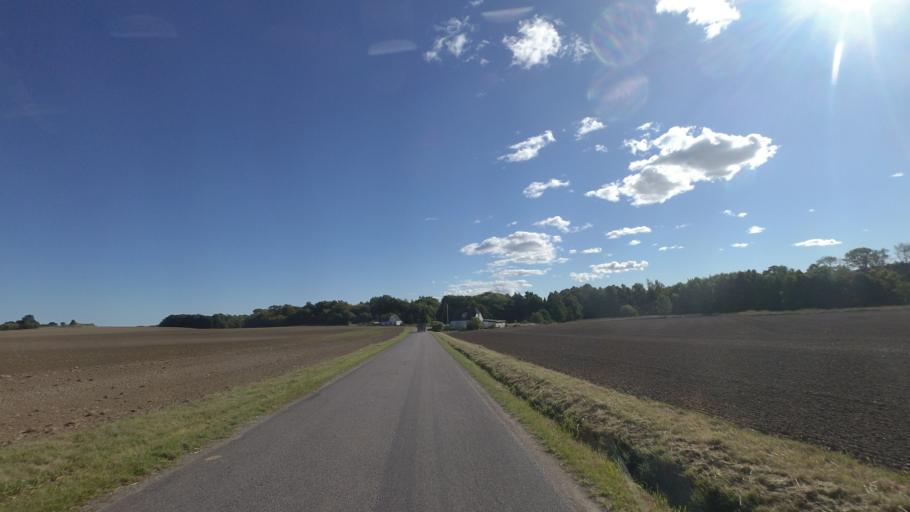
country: DK
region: Capital Region
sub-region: Bornholm Kommune
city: Akirkeby
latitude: 55.1348
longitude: 15.0196
